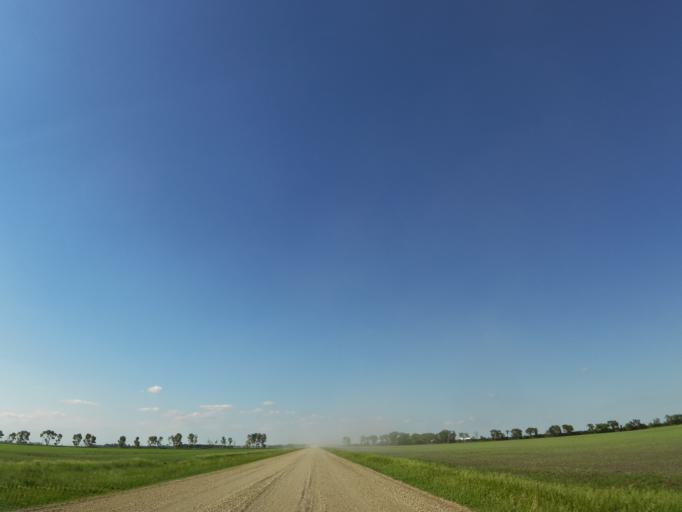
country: US
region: North Dakota
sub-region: Walsh County
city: Grafton
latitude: 48.3259
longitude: -97.2554
